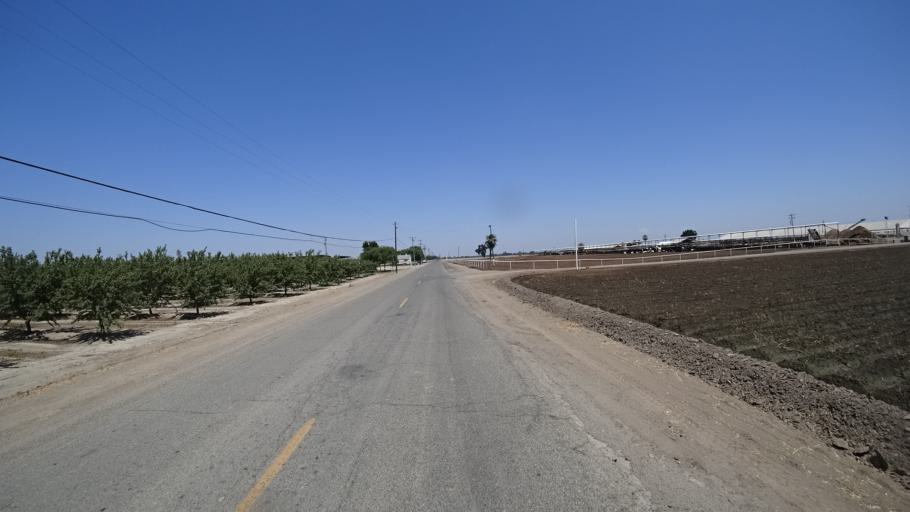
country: US
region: California
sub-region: Kings County
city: Lucerne
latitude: 36.3819
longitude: -119.7270
